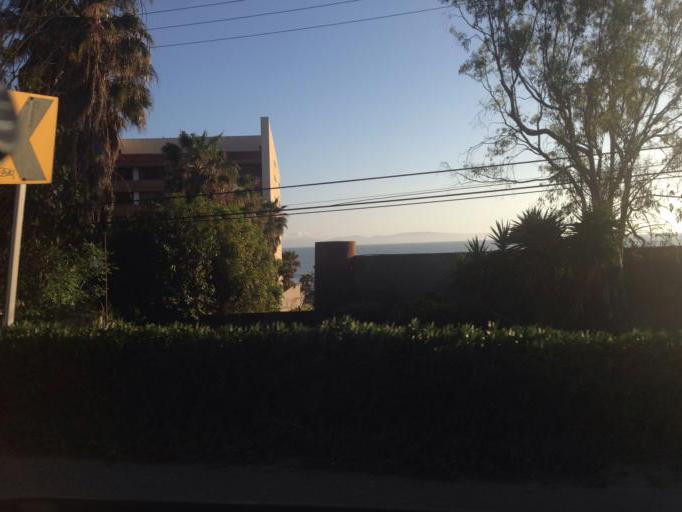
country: MX
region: Baja California
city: Ensenada
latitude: 31.8616
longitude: -116.6503
